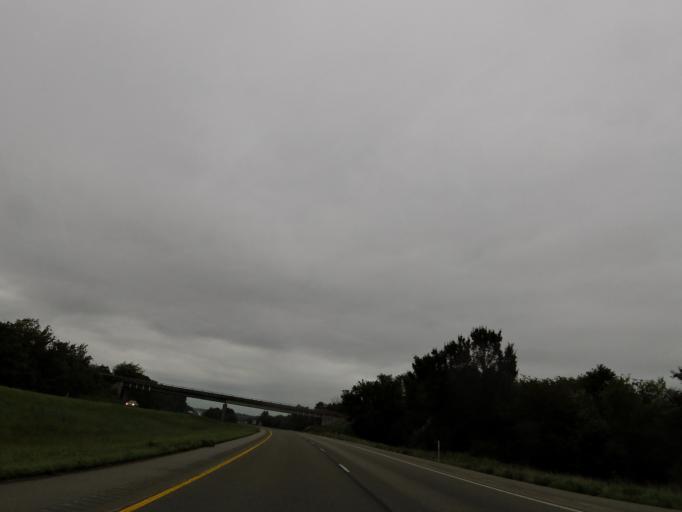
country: US
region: Illinois
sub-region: Johnson County
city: Vienna
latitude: 37.3538
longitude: -88.7885
